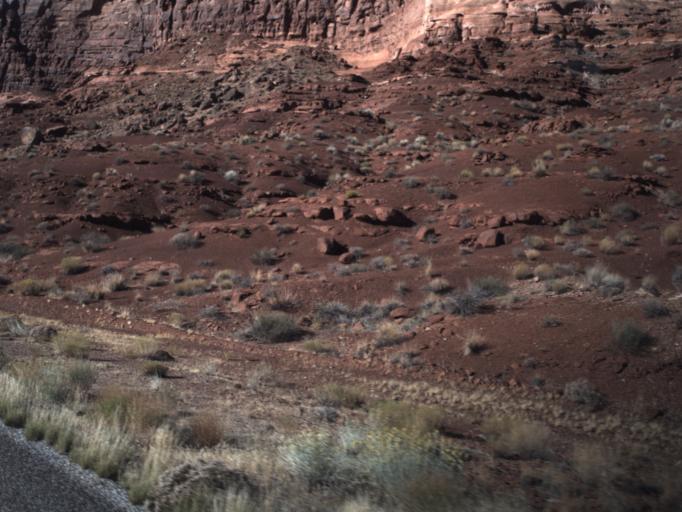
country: US
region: Utah
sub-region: San Juan County
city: Blanding
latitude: 37.9114
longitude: -110.3990
